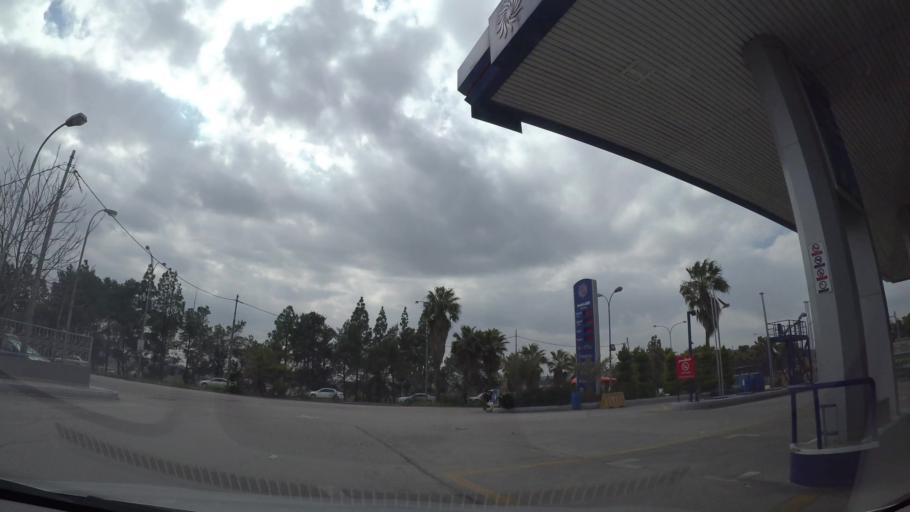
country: JO
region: Balqa
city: As Salt
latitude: 32.0387
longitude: 35.7892
